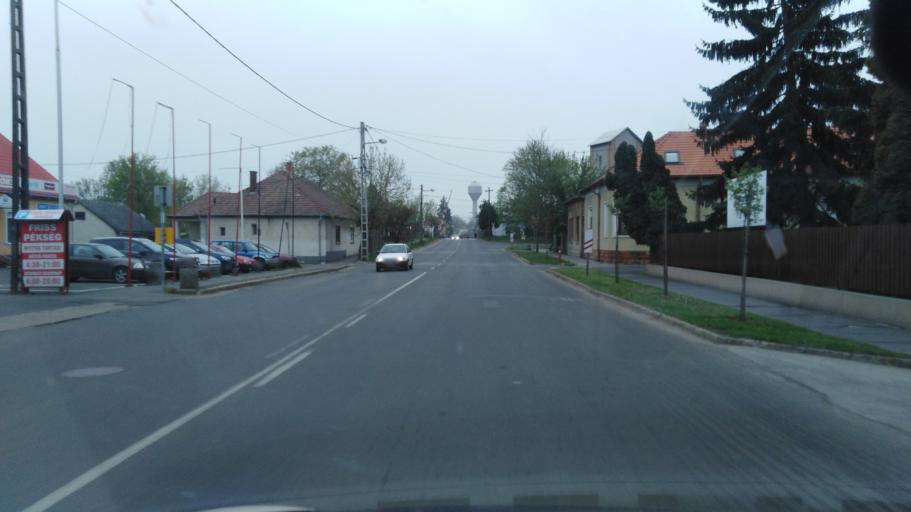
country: HU
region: Nograd
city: Balassagyarmat
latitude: 48.0733
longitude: 19.2963
